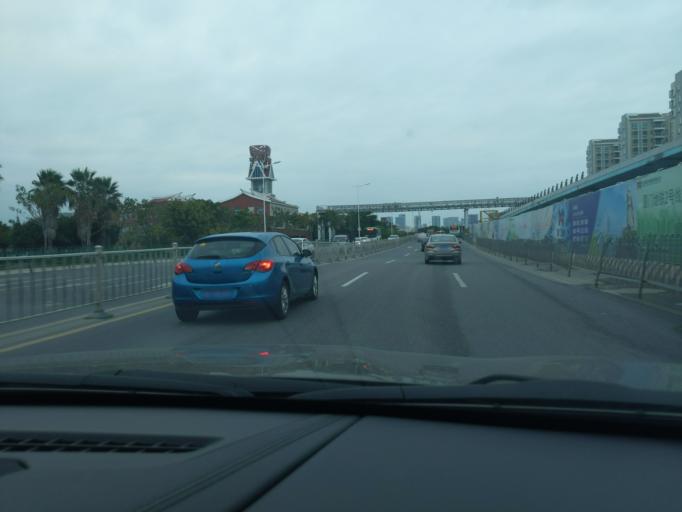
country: CN
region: Fujian
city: Liuwudian
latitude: 24.5350
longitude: 118.1628
